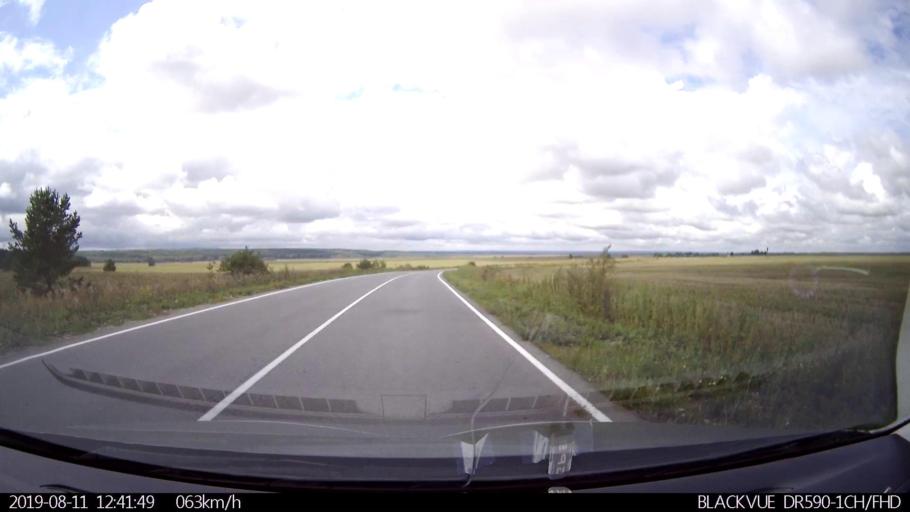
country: RU
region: Ulyanovsk
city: Ignatovka
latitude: 53.8421
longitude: 47.7597
